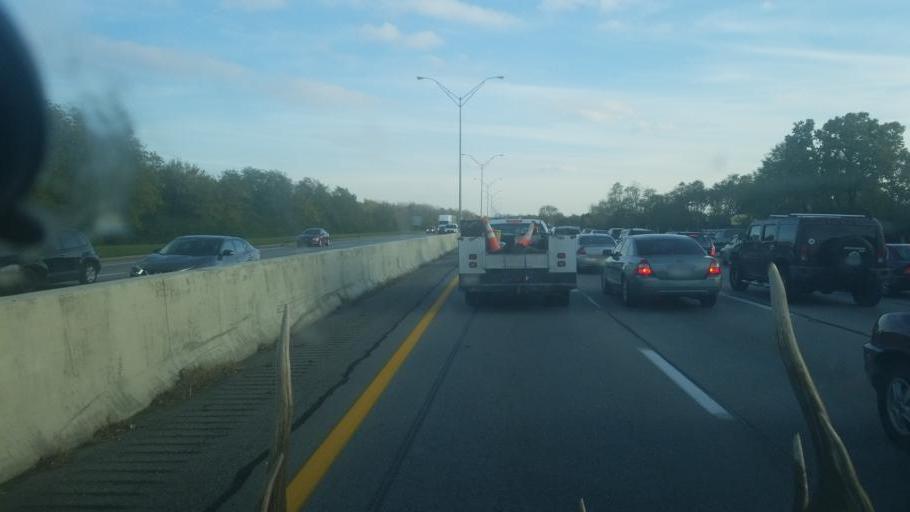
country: US
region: Ohio
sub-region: Franklin County
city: Bexley
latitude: 39.9442
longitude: -82.9418
